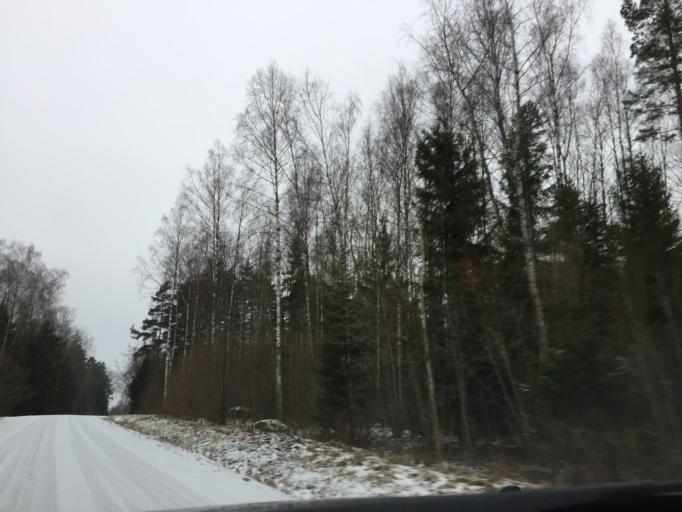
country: LV
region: Salacgrivas
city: Salacgriva
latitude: 57.5188
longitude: 24.3871
